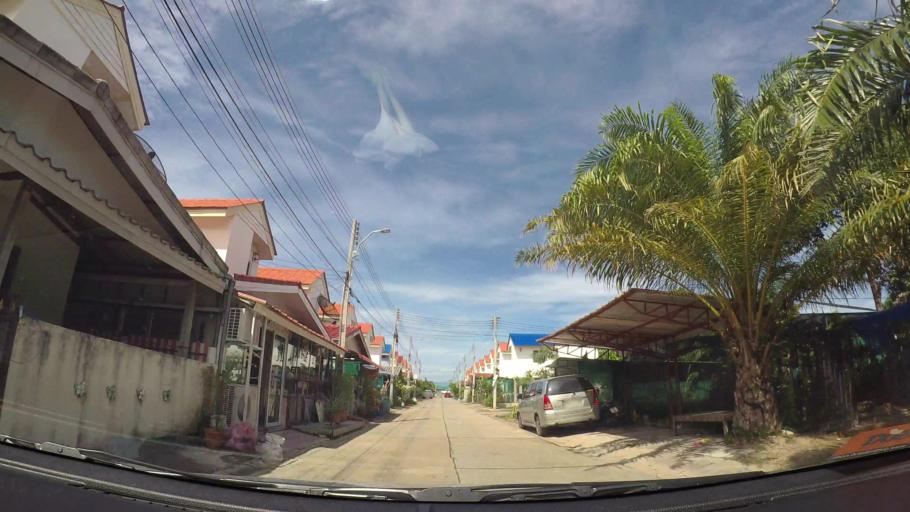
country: TH
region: Chon Buri
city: Sattahip
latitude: 12.6680
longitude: 100.9539
